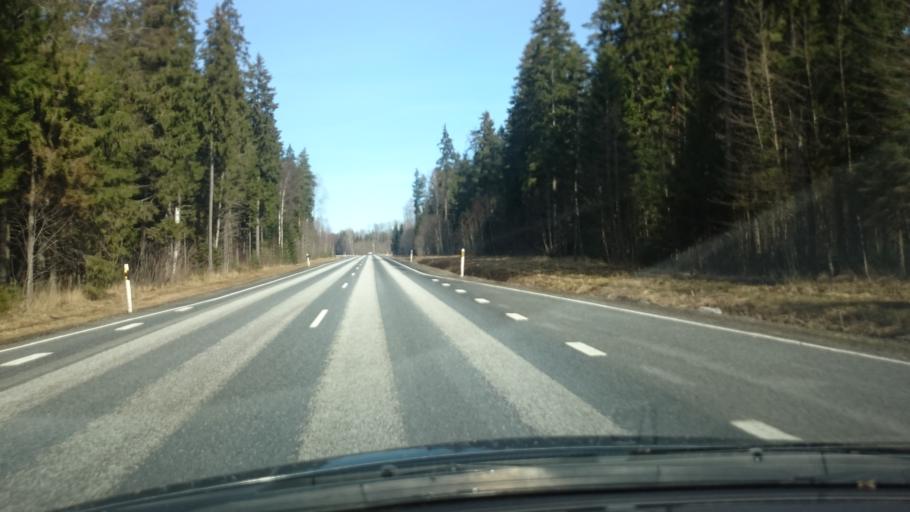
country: EE
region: Jaervamaa
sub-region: Tueri vald
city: Sarevere
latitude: 58.7182
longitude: 25.2757
